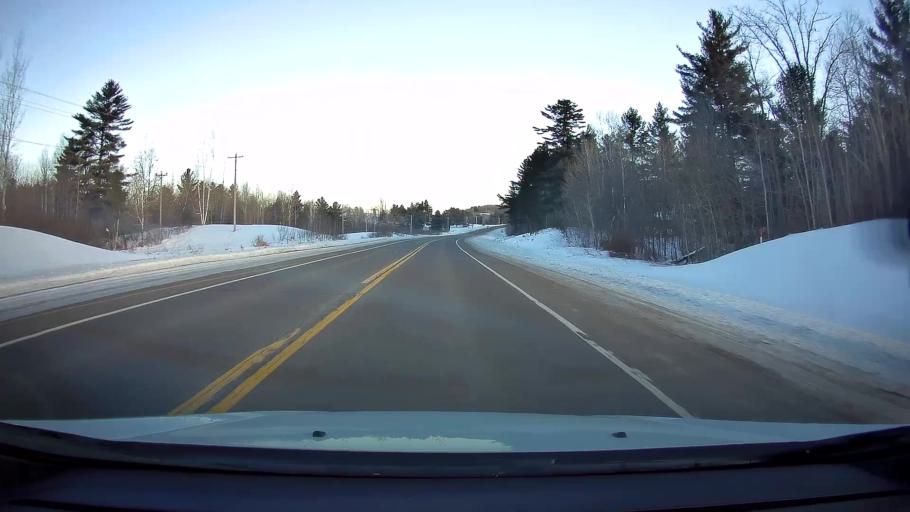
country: US
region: Wisconsin
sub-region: Barron County
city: Cumberland
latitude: 45.5968
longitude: -92.0176
